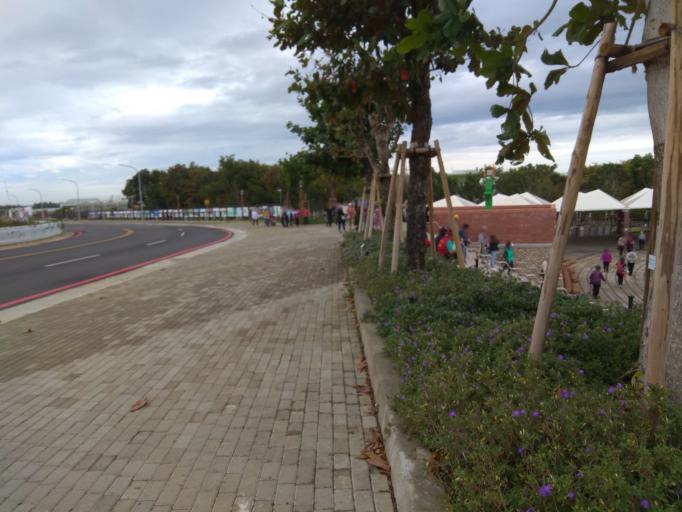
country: TW
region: Taiwan
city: Fengyuan
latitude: 24.3240
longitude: 120.6850
